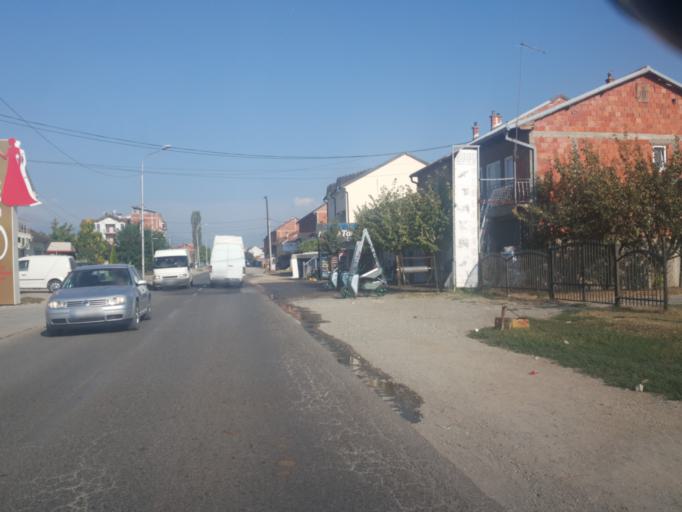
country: XK
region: Gjakova
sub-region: Komuna e Gjakoves
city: Gjakove
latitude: 42.3997
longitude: 20.4166
